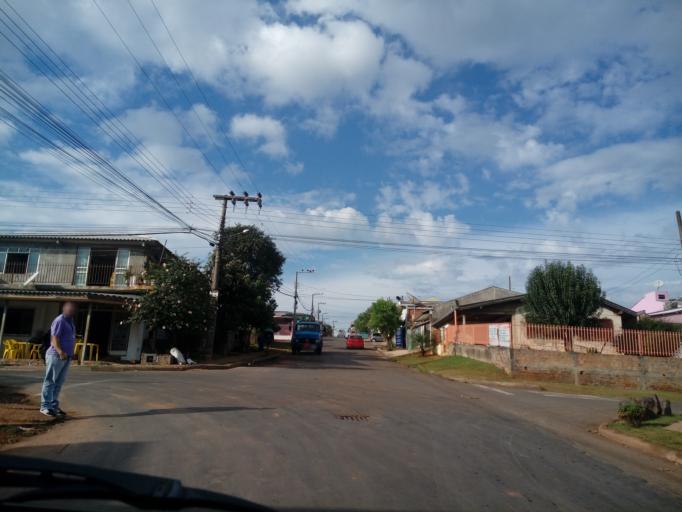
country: BR
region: Santa Catarina
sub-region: Chapeco
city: Chapeco
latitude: -27.0965
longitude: -52.5908
